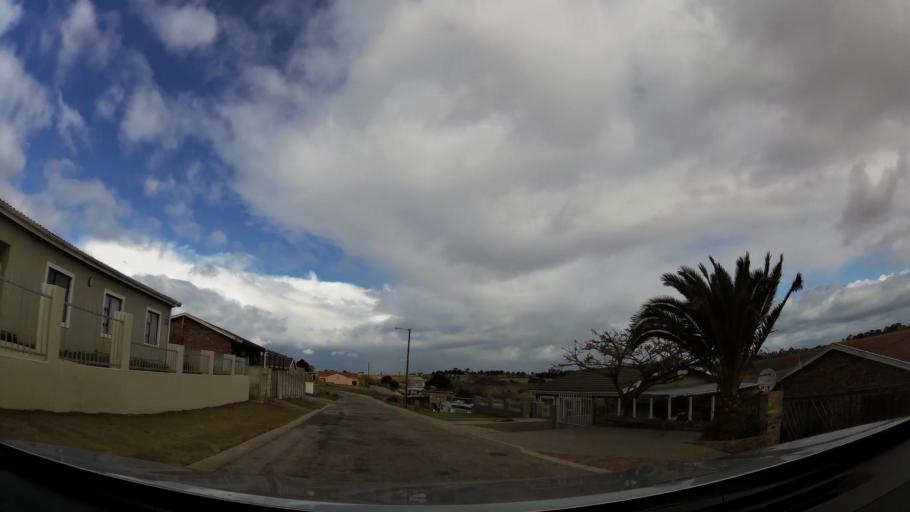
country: ZA
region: Western Cape
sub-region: Eden District Municipality
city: George
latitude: -34.0244
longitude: 22.4752
